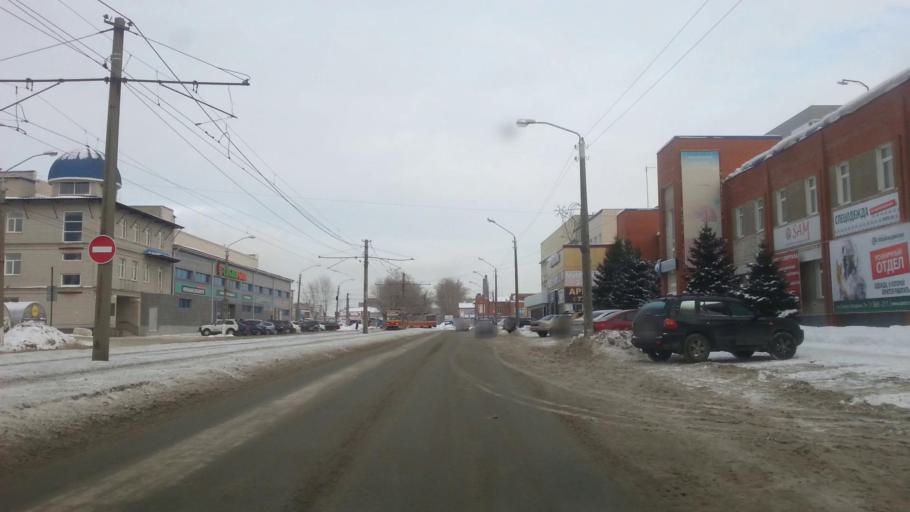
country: RU
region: Altai Krai
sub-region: Gorod Barnaulskiy
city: Barnaul
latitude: 53.3744
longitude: 83.7529
